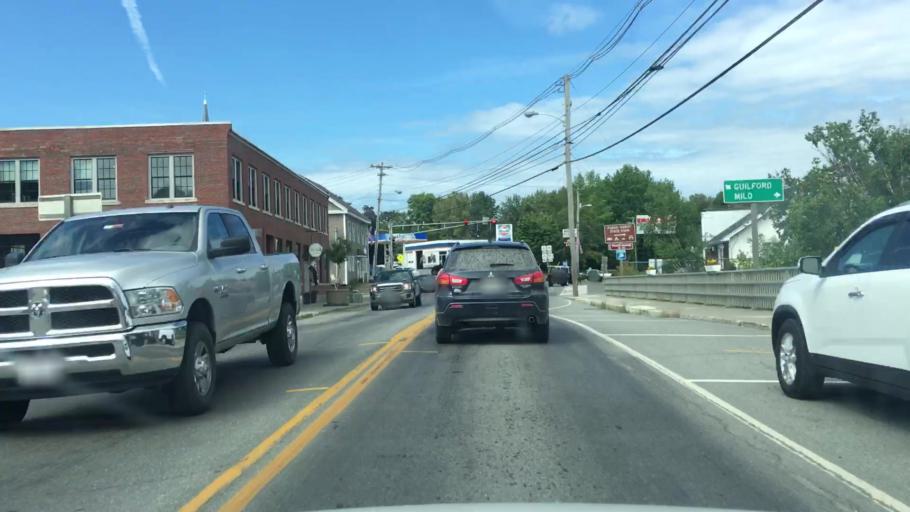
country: US
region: Maine
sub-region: Piscataquis County
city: Dover-Foxcroft
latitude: 45.1841
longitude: -69.2298
